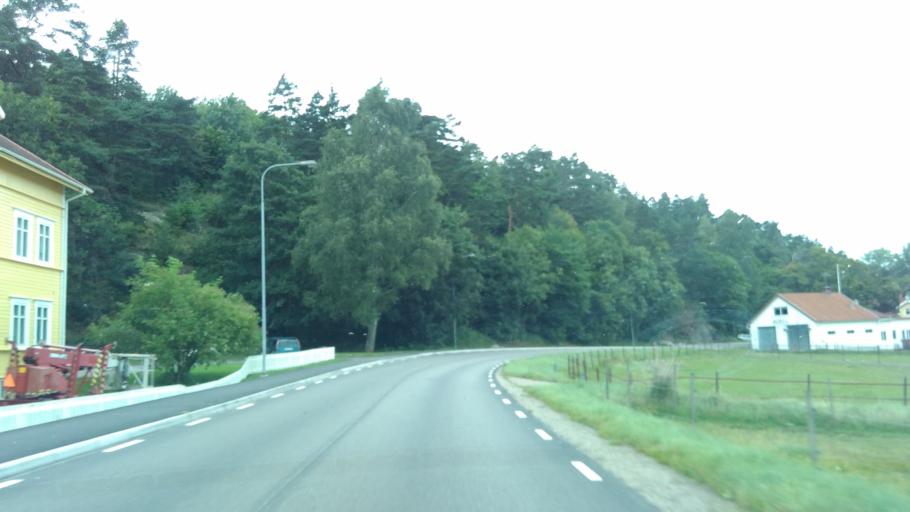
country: SE
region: Vaestra Goetaland
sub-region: Marks Kommun
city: Fritsla
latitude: 57.5590
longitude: 12.7841
